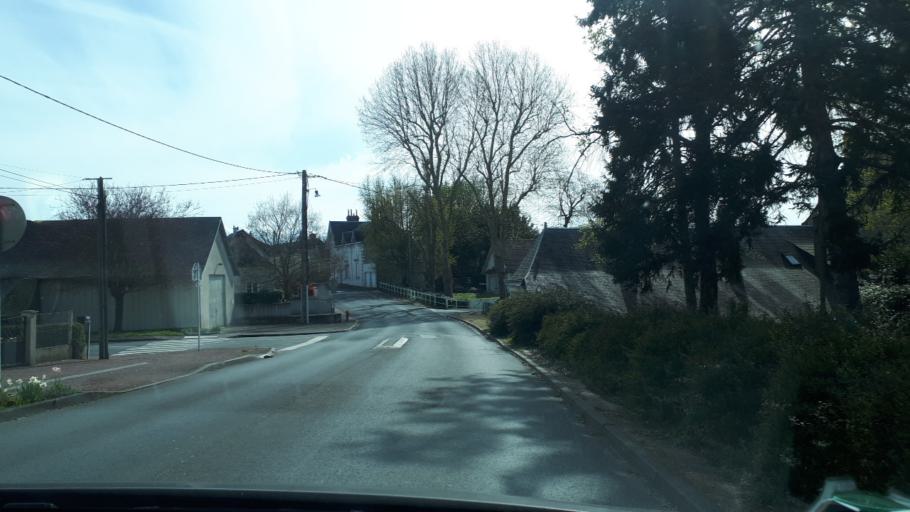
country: FR
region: Pays de la Loire
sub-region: Departement de la Sarthe
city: Yvre-le-Polin
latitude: 47.8182
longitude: 0.1502
